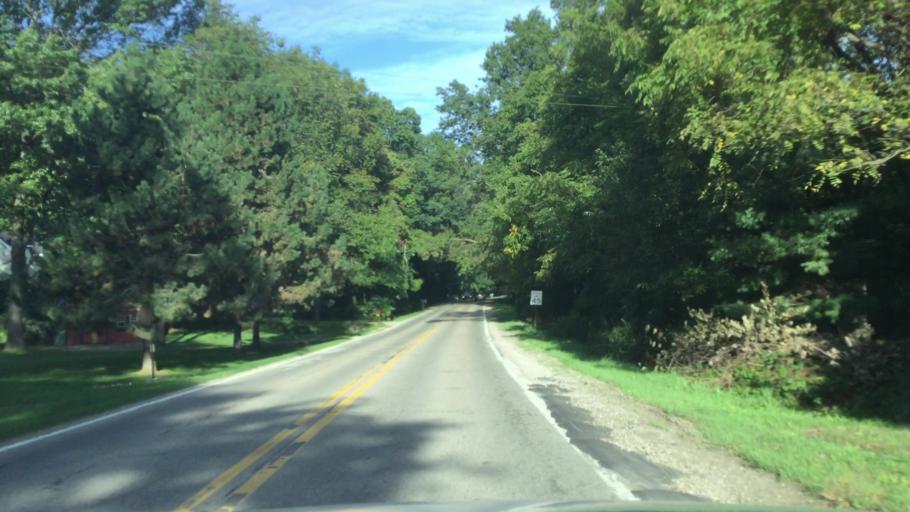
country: US
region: Michigan
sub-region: Livingston County
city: Brighton
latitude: 42.4782
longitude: -83.8421
